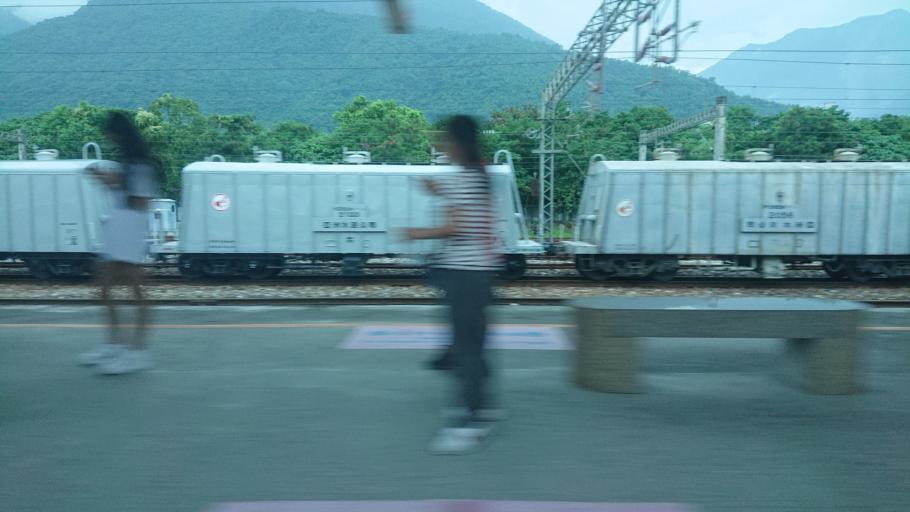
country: TW
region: Taiwan
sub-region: Hualien
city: Hualian
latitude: 24.1279
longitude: 121.6403
